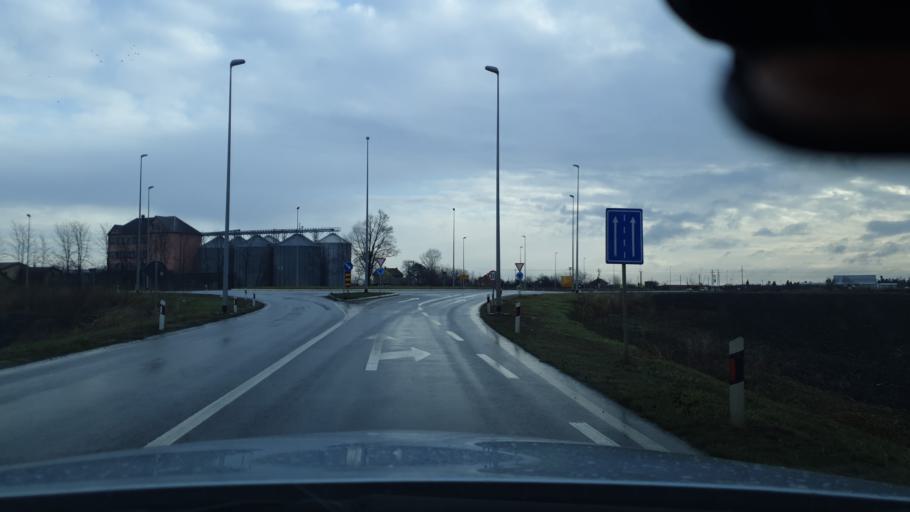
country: RS
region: Autonomna Pokrajina Vojvodina
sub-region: Juznobanatski Okrug
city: Kovin
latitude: 44.8101
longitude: 20.8869
